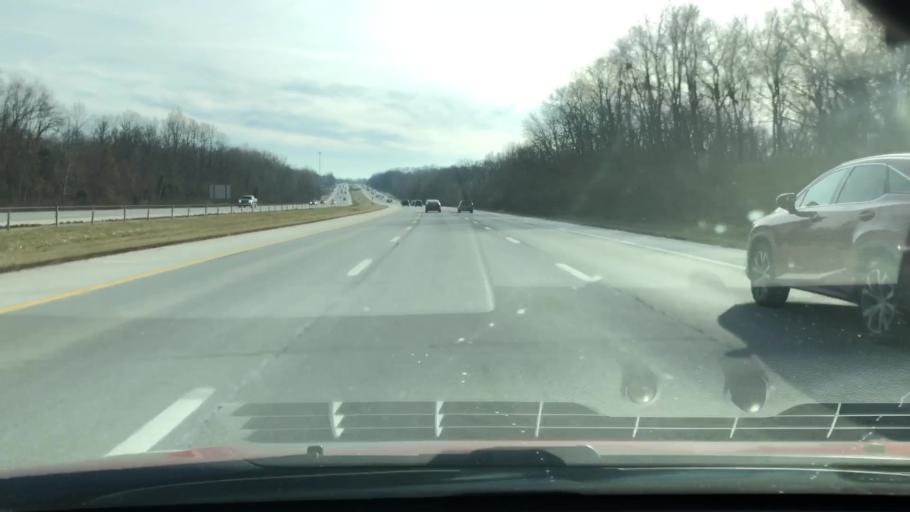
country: US
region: Ohio
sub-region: Greene County
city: Beavercreek
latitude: 39.6819
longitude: -84.1005
